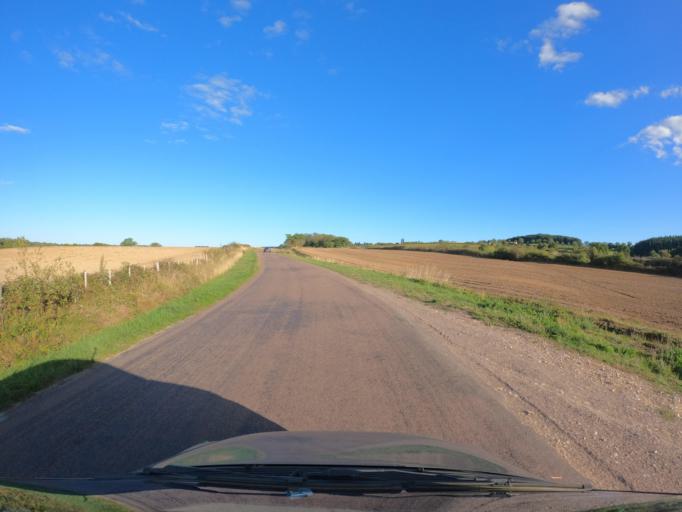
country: FR
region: Bourgogne
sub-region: Departement de Saone-et-Loire
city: Ecuisses
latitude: 46.7451
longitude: 4.5436
